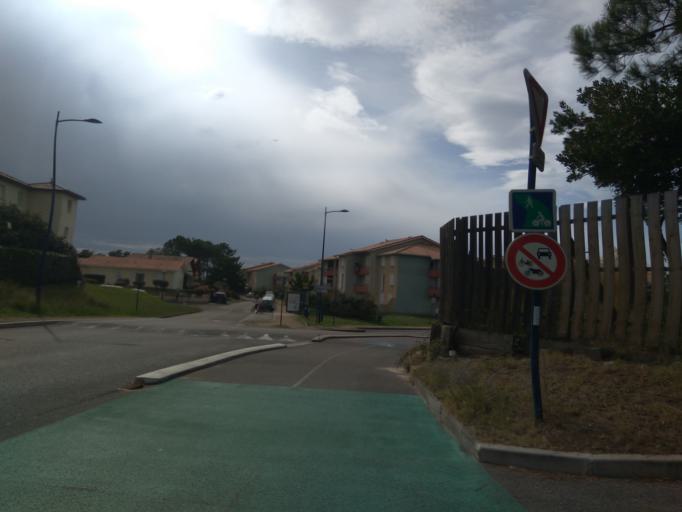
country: FR
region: Aquitaine
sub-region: Departement des Landes
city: Capbreton
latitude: 43.6350
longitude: -1.4438
